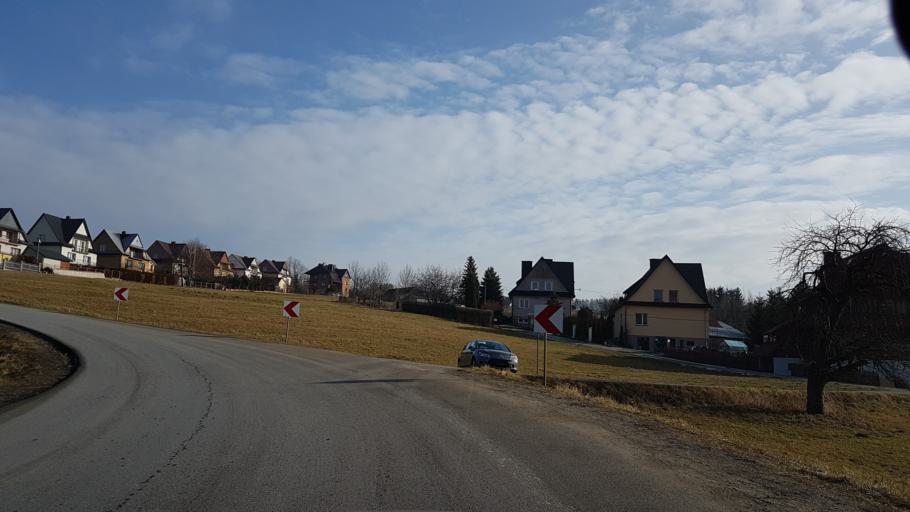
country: PL
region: Lesser Poland Voivodeship
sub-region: Powiat limanowski
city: Lukowica
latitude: 49.6405
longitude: 20.5052
